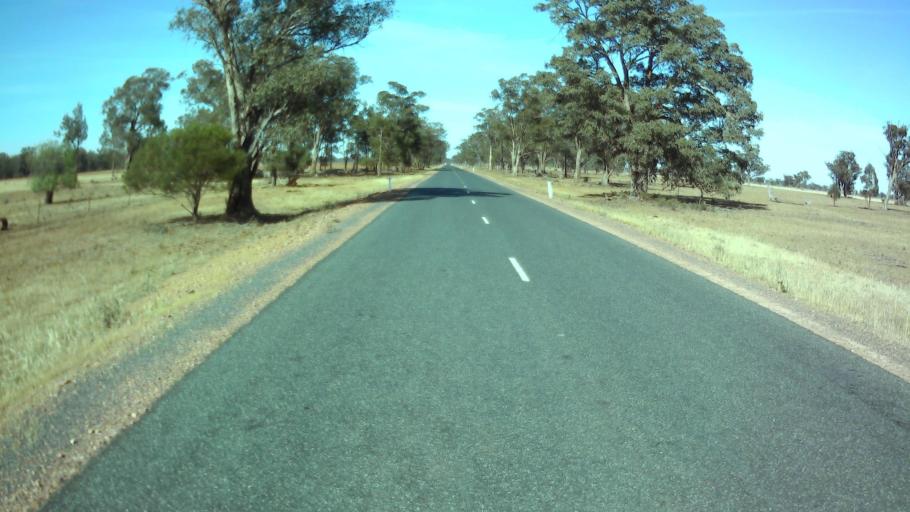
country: AU
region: New South Wales
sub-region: Weddin
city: Grenfell
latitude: -34.1010
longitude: 147.8756
